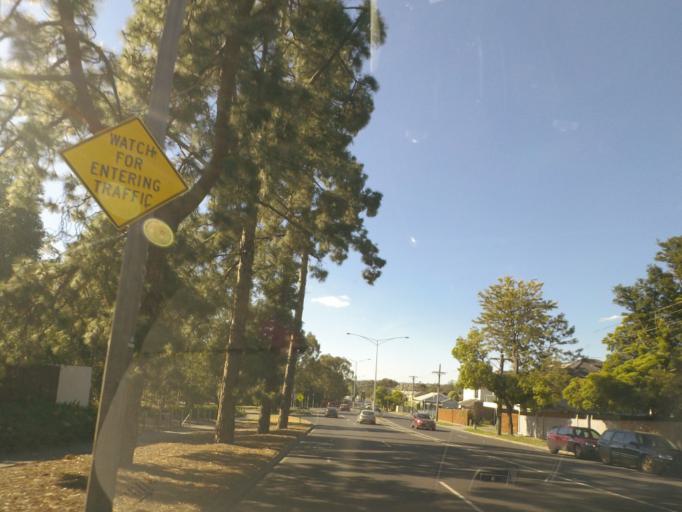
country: AU
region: Victoria
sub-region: Boroondara
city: Kew
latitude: -37.7955
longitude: 145.0309
